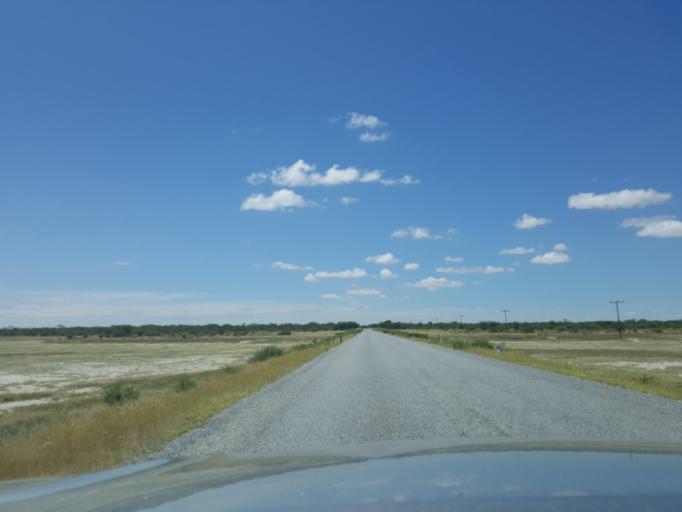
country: BW
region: Central
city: Nata
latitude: -20.1451
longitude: 25.7225
